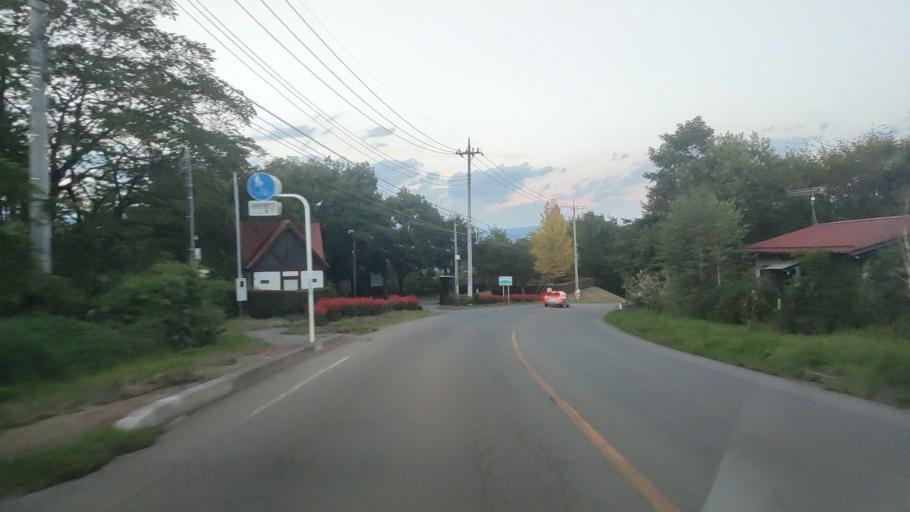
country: JP
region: Gunma
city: Nakanojomachi
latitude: 36.5285
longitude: 138.6040
